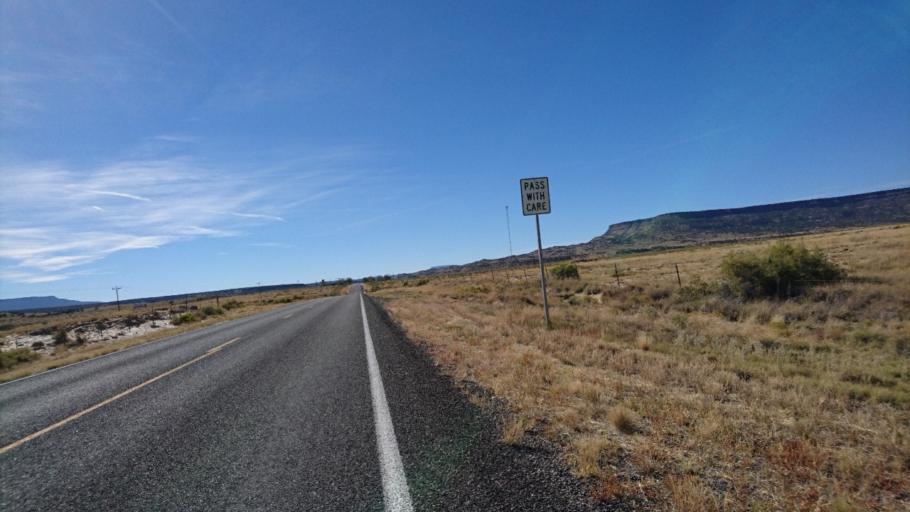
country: US
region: New Mexico
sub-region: Cibola County
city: Skyline-Ganipa
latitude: 35.0801
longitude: -107.6370
